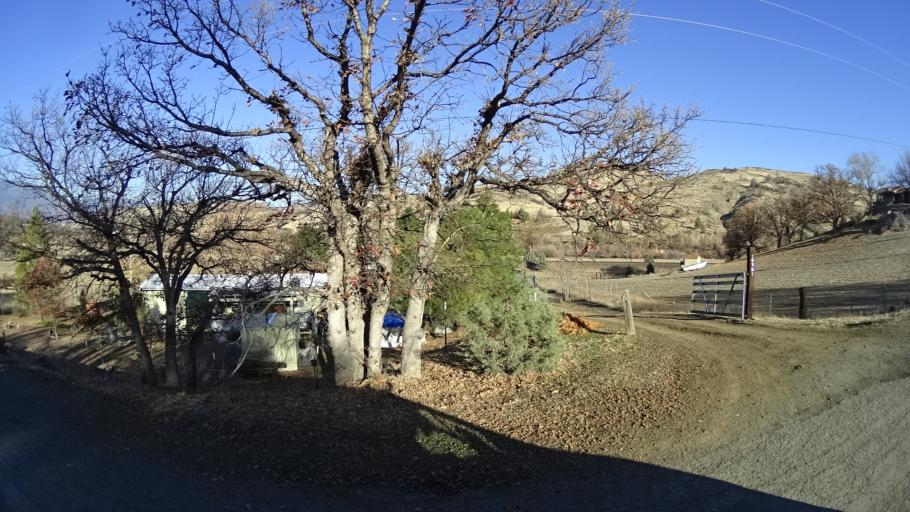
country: US
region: California
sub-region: Siskiyou County
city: Montague
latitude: 41.8967
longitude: -122.4933
